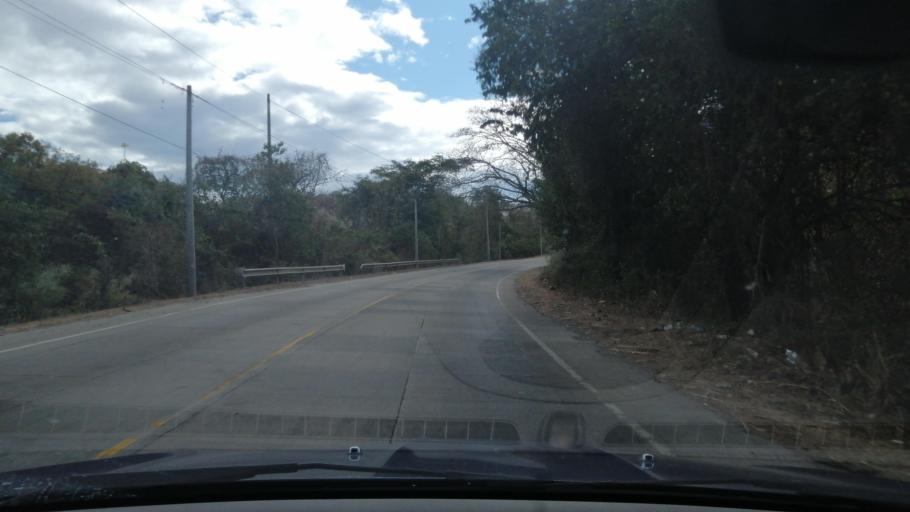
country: SV
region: Santa Ana
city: Texistepeque
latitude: 14.0659
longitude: -89.5042
